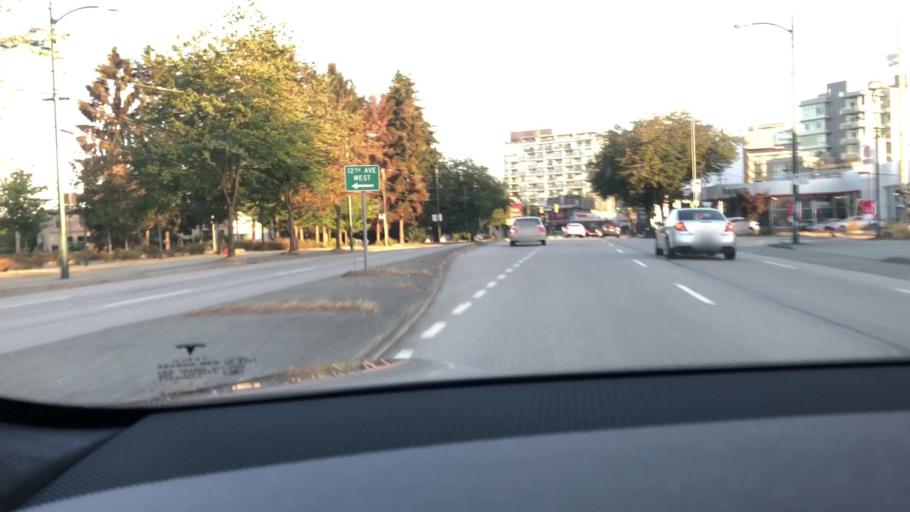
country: CA
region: British Columbia
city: Vancouver
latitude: 49.2587
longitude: -123.0947
